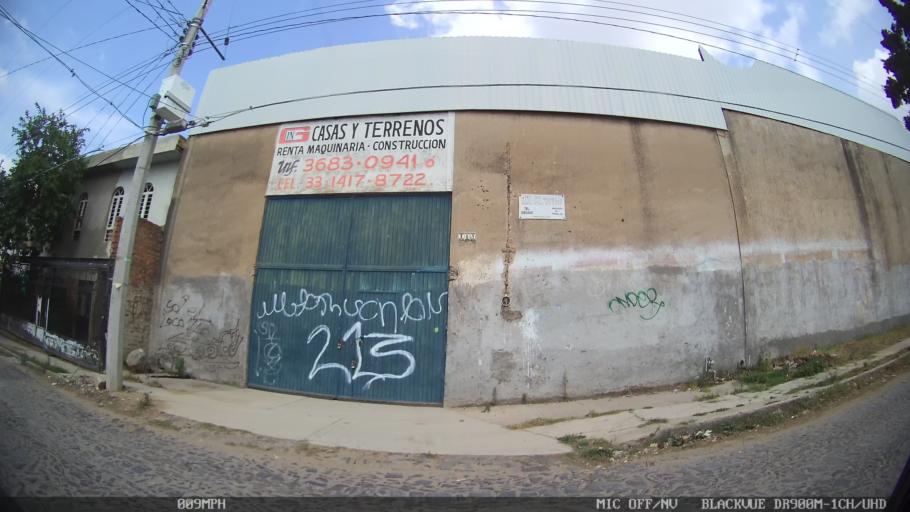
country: MX
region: Jalisco
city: Tonala
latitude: 20.6253
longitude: -103.2313
